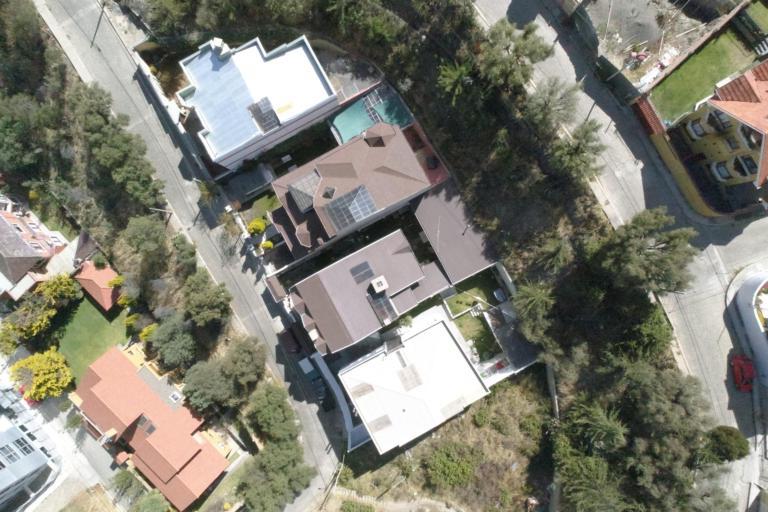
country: BO
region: La Paz
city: La Paz
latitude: -16.5346
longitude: -68.0694
